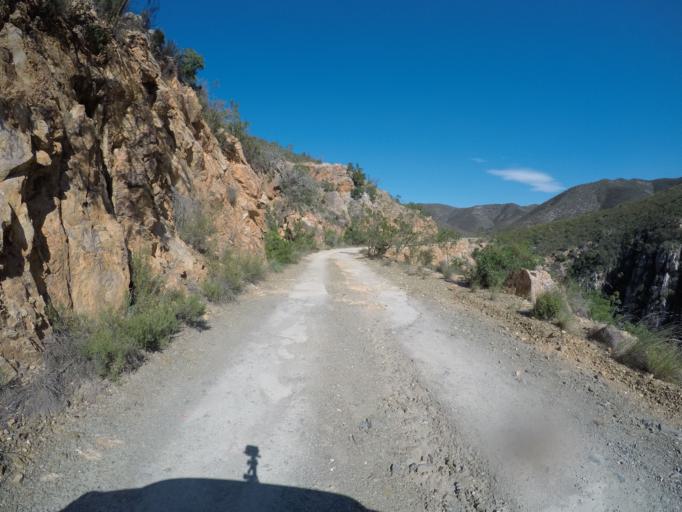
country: ZA
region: Eastern Cape
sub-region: Cacadu District Municipality
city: Kareedouw
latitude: -33.6522
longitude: 24.5037
